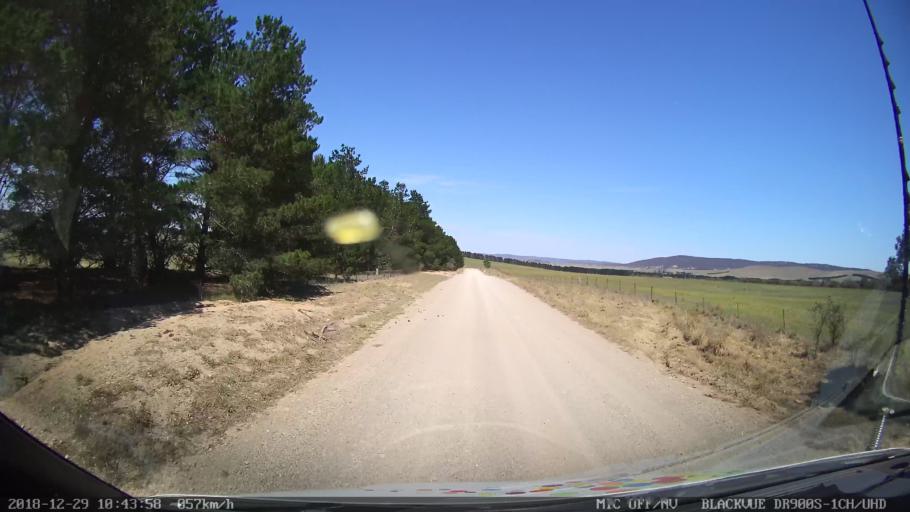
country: AU
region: New South Wales
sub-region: Palerang
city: Bungendore
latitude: -35.0412
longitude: 149.5330
